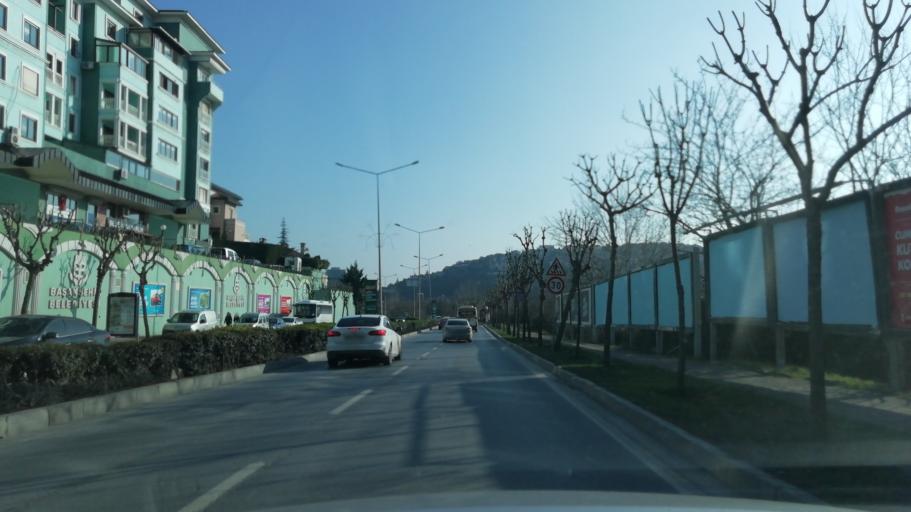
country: TR
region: Istanbul
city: Esenyurt
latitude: 41.0714
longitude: 28.6935
